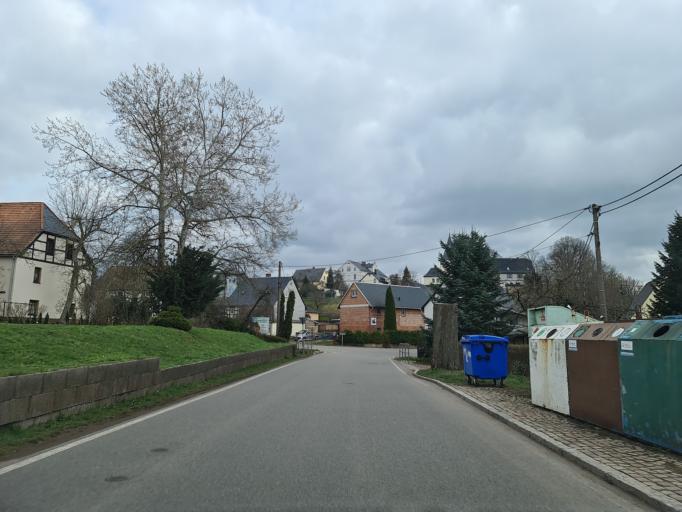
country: DE
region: Saxony
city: Wildenfels
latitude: 50.6768
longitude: 12.6085
